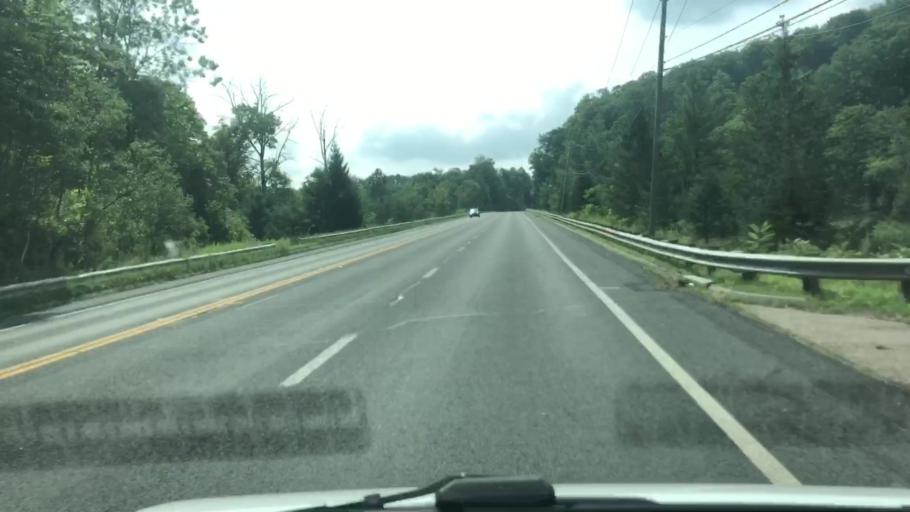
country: US
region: Massachusetts
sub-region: Berkshire County
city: Lanesborough
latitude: 42.5977
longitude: -73.2427
